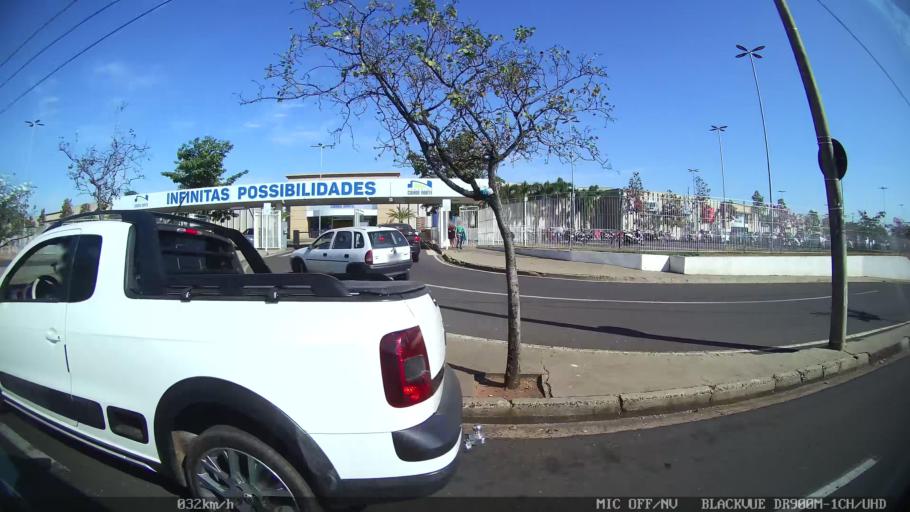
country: BR
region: Sao Paulo
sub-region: Sao Jose Do Rio Preto
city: Sao Jose do Rio Preto
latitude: -20.7696
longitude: -49.3850
